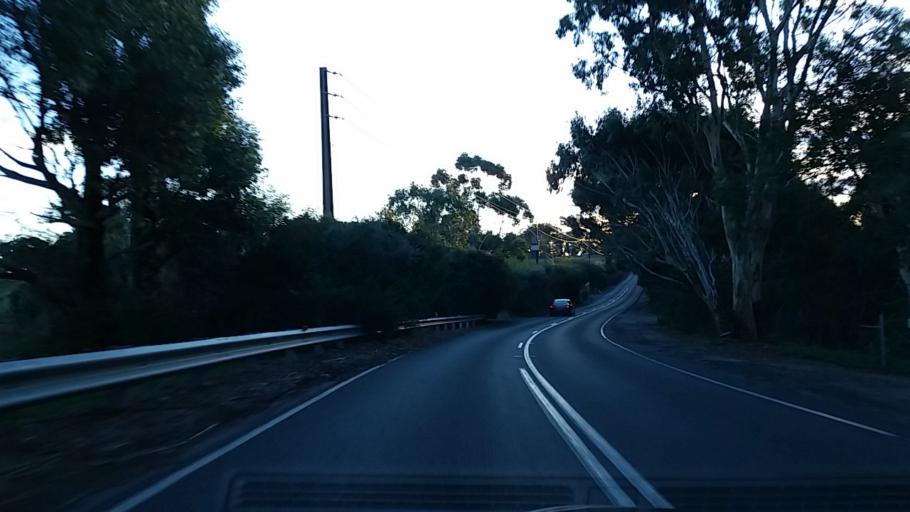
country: AU
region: South Australia
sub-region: Onkaparinga
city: Craigburn Farm
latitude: -35.0709
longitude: 138.6342
